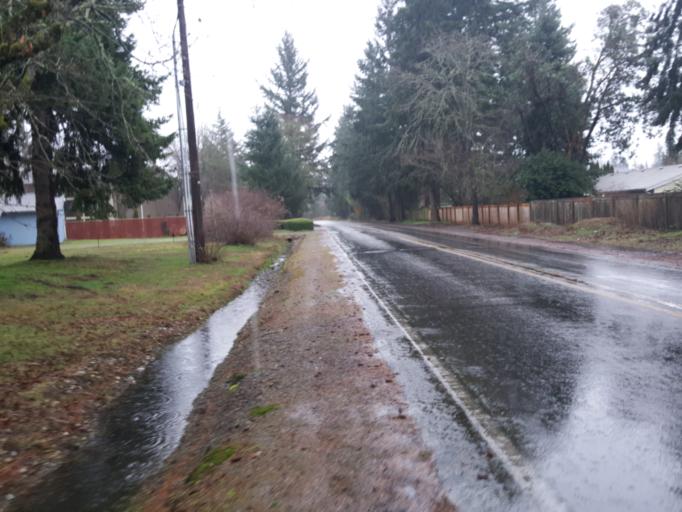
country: US
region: Washington
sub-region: Pierce County
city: Lakewood
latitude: 47.2000
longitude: -122.5347
